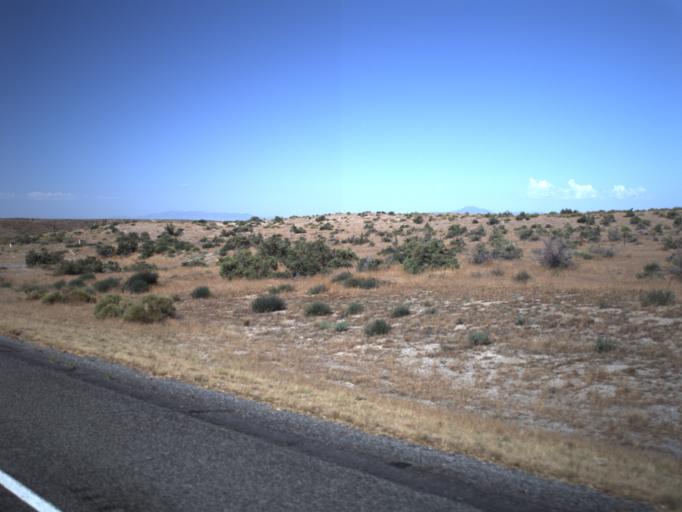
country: US
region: Utah
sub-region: Millard County
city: Delta
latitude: 39.4047
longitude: -112.4940
